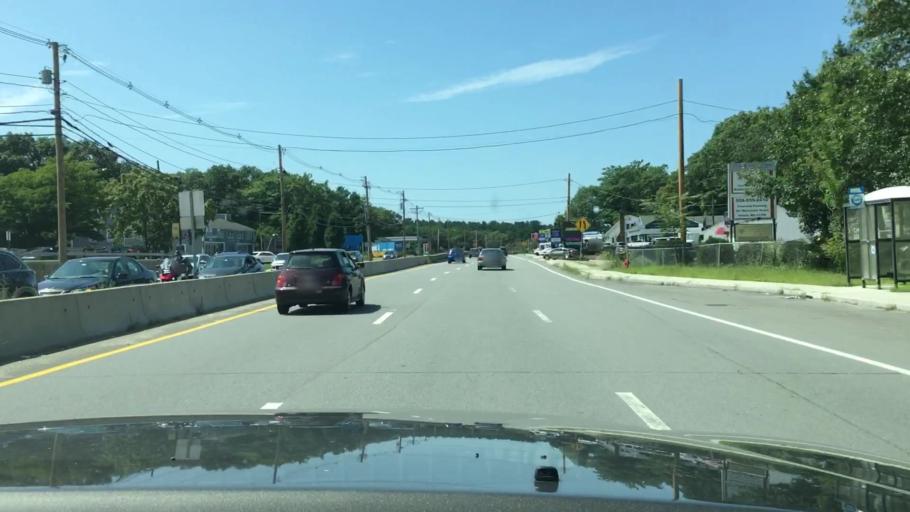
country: US
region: Massachusetts
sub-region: Middlesex County
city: Natick
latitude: 42.3035
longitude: -71.3327
